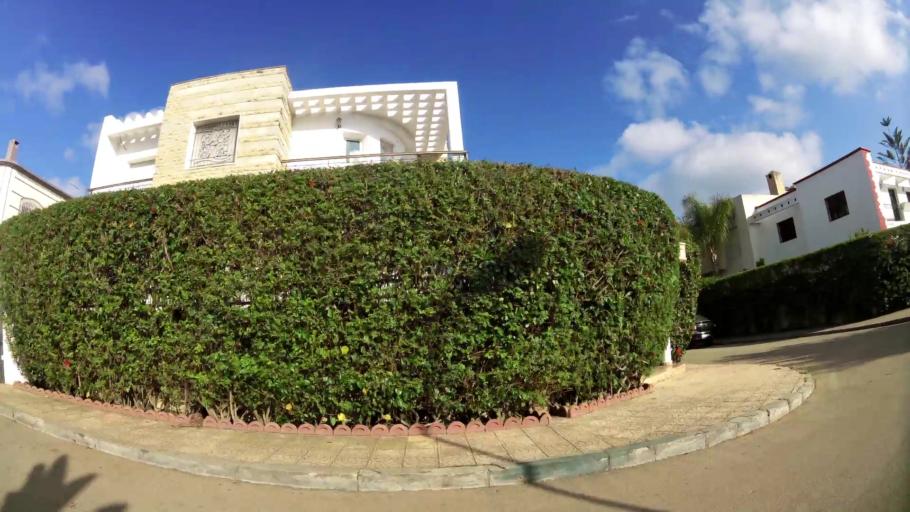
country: MA
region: Rabat-Sale-Zemmour-Zaer
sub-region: Skhirate-Temara
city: Temara
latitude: 33.9517
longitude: -6.8579
